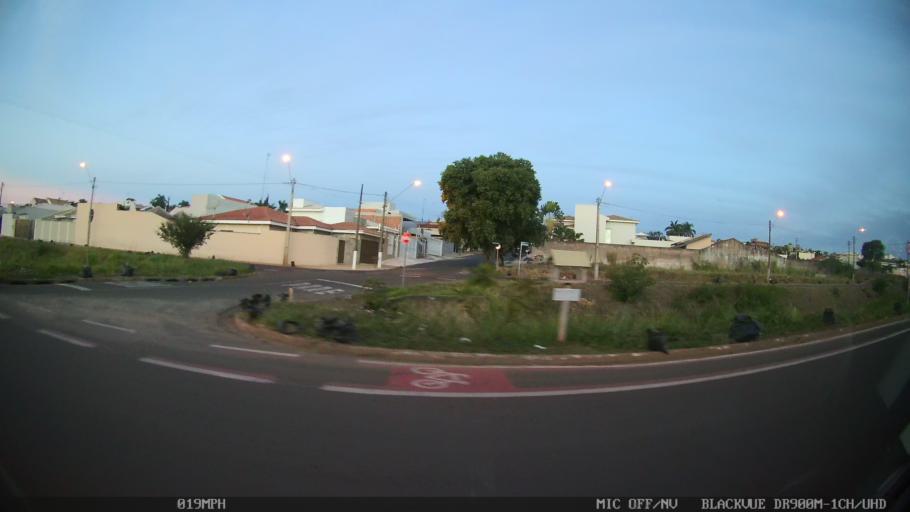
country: BR
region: Sao Paulo
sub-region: Catanduva
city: Catanduva
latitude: -21.1452
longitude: -48.9913
